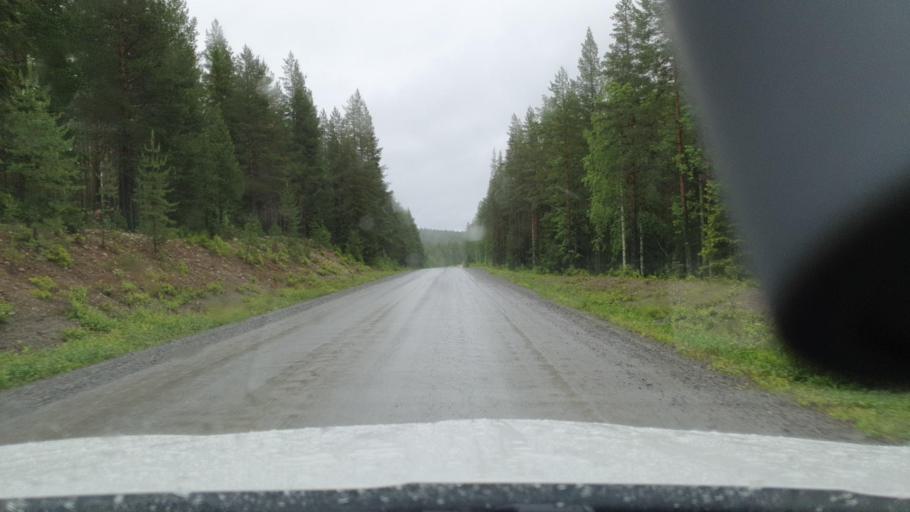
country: SE
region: Vaesterbotten
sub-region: Skelleftea Kommun
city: Burtraesk
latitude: 64.3806
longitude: 20.3358
